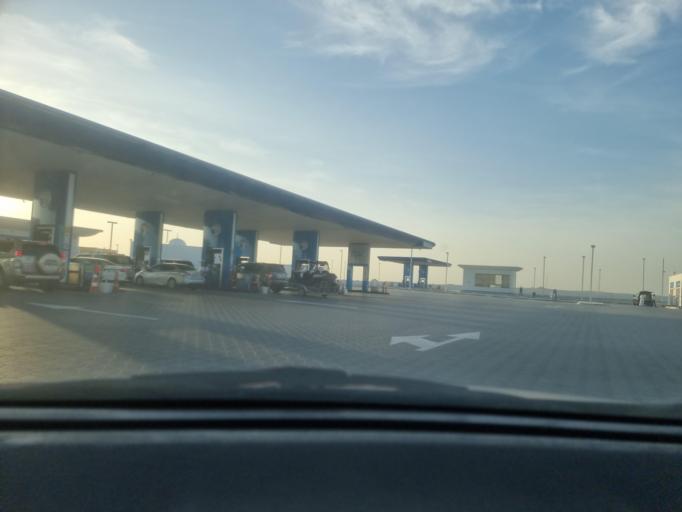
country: AE
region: Abu Dhabi
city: Abu Dhabi
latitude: 24.3163
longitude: 54.6781
